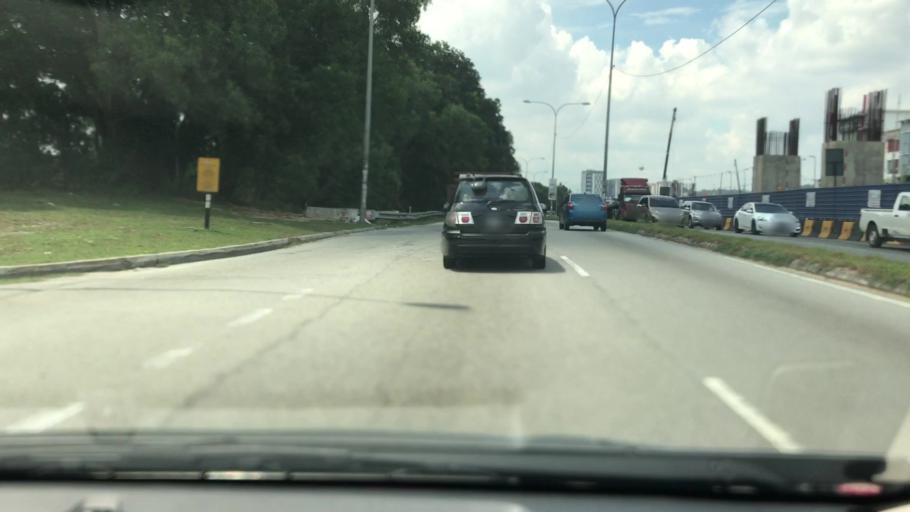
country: MY
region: Putrajaya
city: Putrajaya
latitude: 2.9832
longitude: 101.6605
